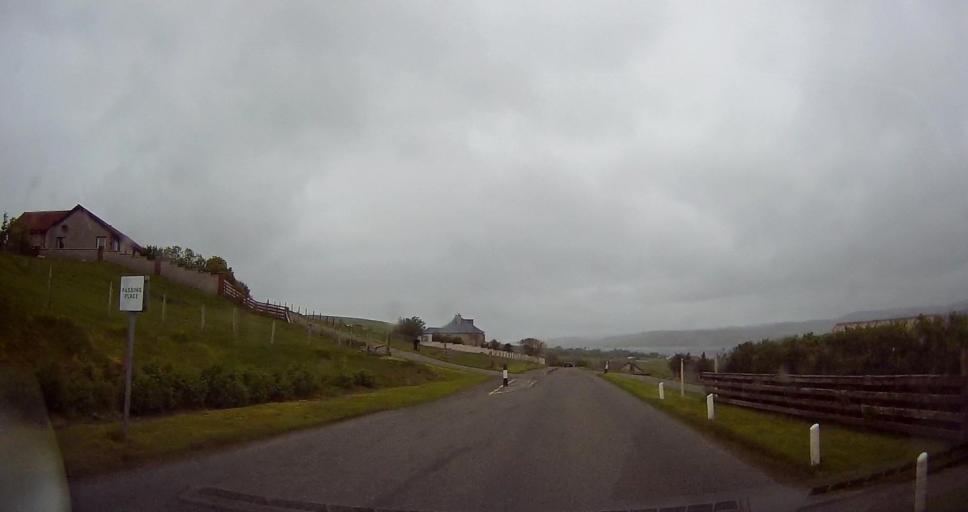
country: GB
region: Scotland
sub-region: Shetland Islands
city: Lerwick
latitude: 60.2789
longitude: -1.3894
